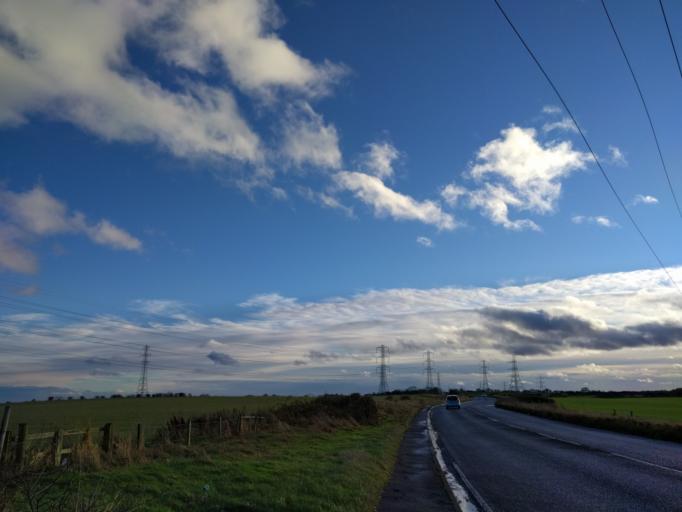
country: GB
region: England
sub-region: Northumberland
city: Bedlington
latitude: 55.1199
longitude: -1.5756
